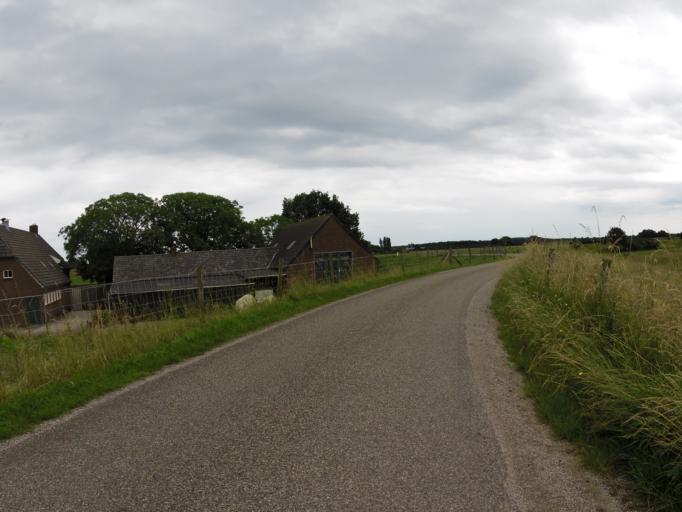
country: NL
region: North Brabant
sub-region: Gemeente Landerd
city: Reek
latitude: 51.7669
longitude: 5.6929
